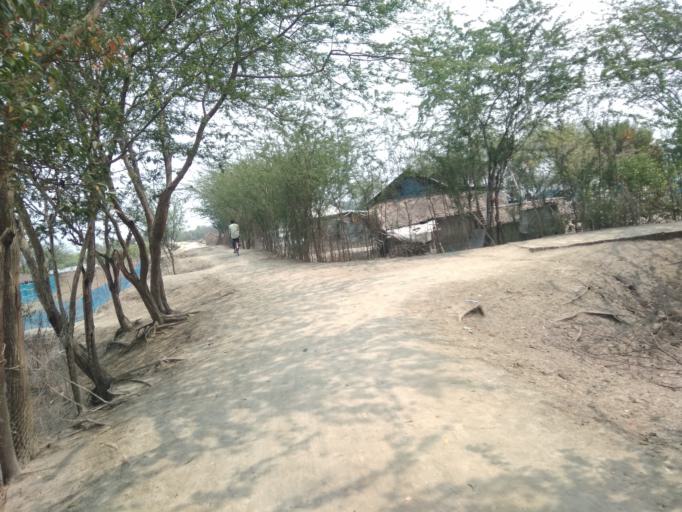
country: IN
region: West Bengal
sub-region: North 24 Parganas
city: Taki
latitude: 22.2813
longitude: 89.2945
